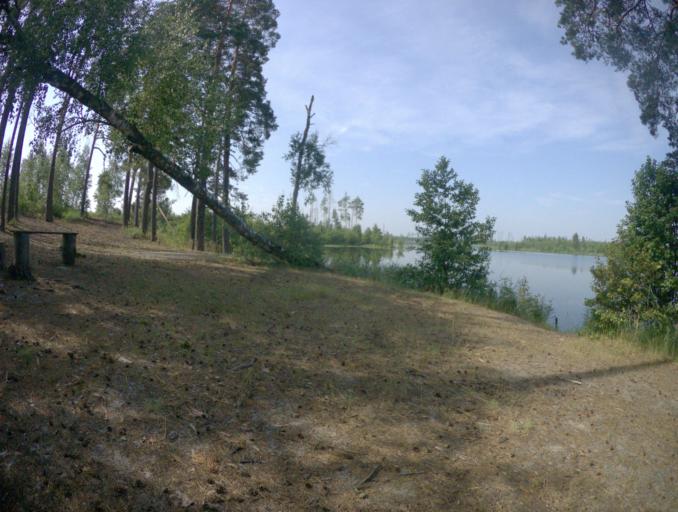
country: RU
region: Ivanovo
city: Talitsy
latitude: 56.4186
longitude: 42.3073
